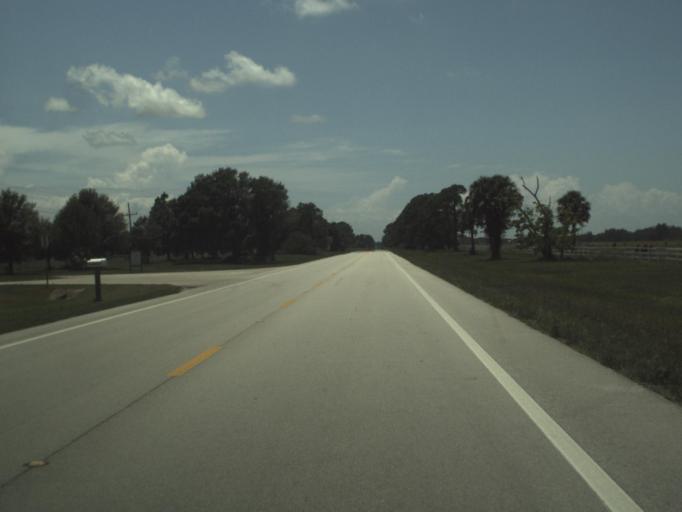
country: US
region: Florida
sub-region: Martin County
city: Indiantown
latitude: 27.0477
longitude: -80.3445
